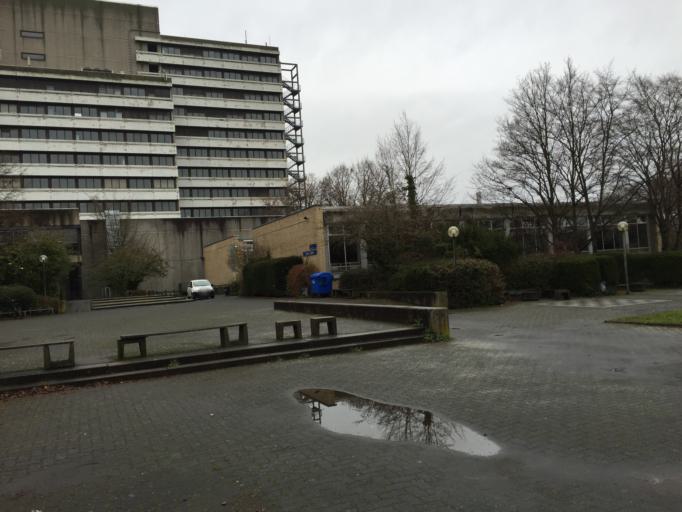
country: DE
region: North Rhine-Westphalia
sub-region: Regierungsbezirk Koln
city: Bonn
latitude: 50.7516
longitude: 7.0973
